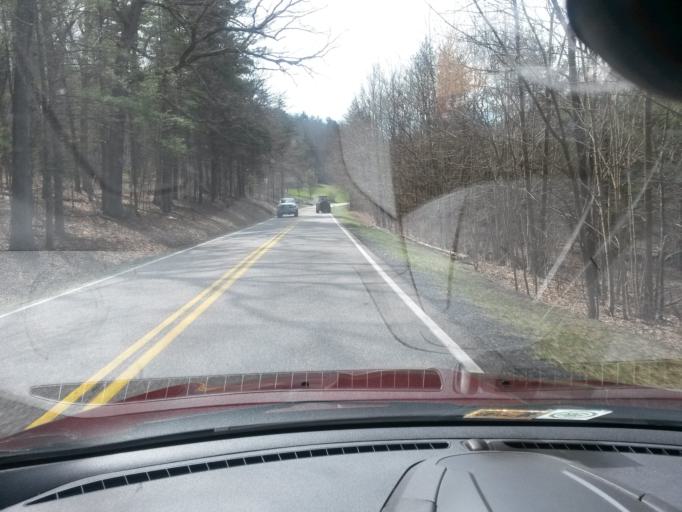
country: US
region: West Virginia
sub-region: Greenbrier County
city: White Sulphur Springs
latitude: 37.6641
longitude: -80.2300
